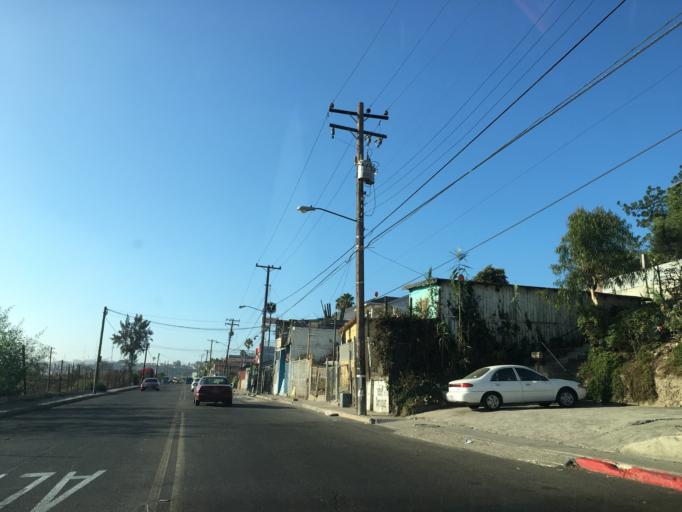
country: MX
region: Baja California
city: Tijuana
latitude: 32.5313
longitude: -117.0639
